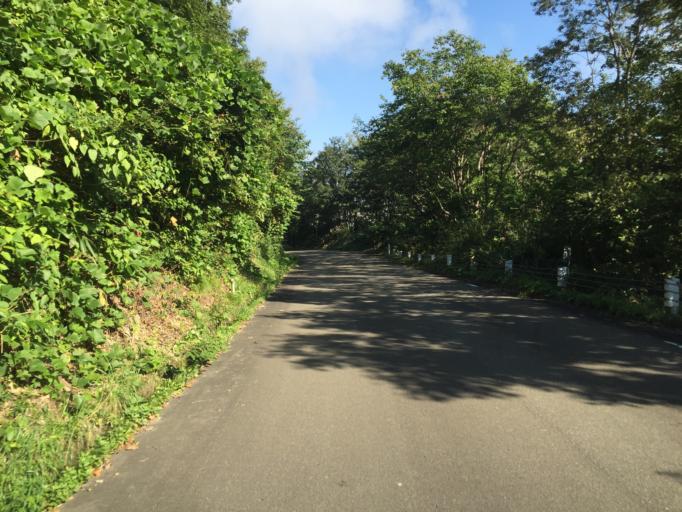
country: JP
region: Fukushima
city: Inawashiro
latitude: 37.4803
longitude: 139.9822
